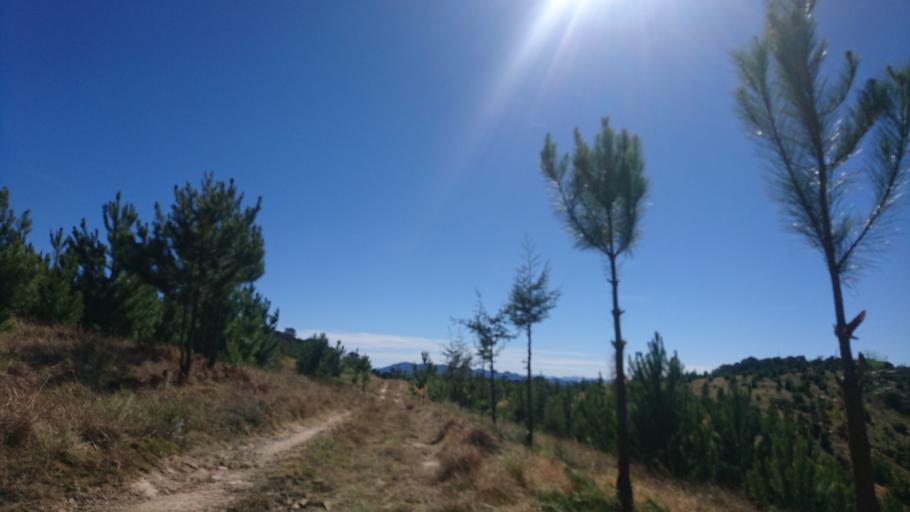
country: MX
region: San Luis Potosi
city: Zaragoza
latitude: 22.0163
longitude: -100.6213
